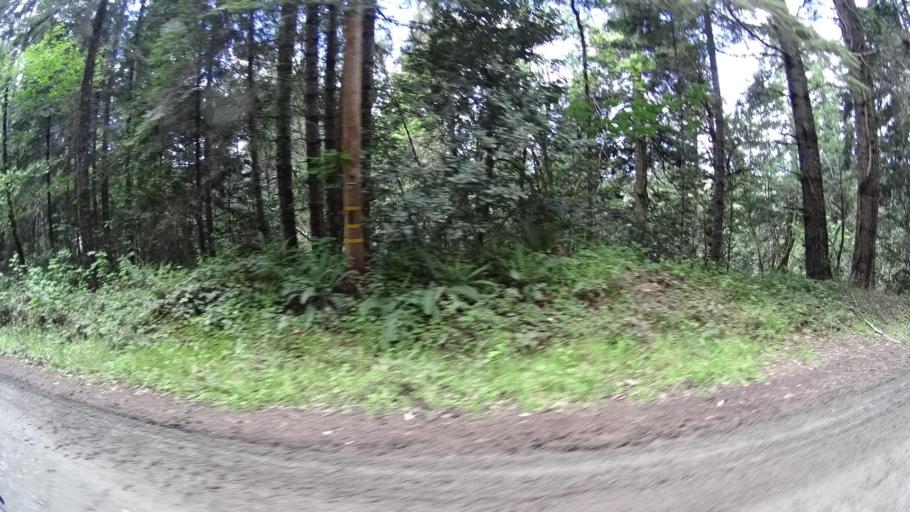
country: US
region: California
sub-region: Humboldt County
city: Blue Lake
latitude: 40.7924
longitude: -123.8779
